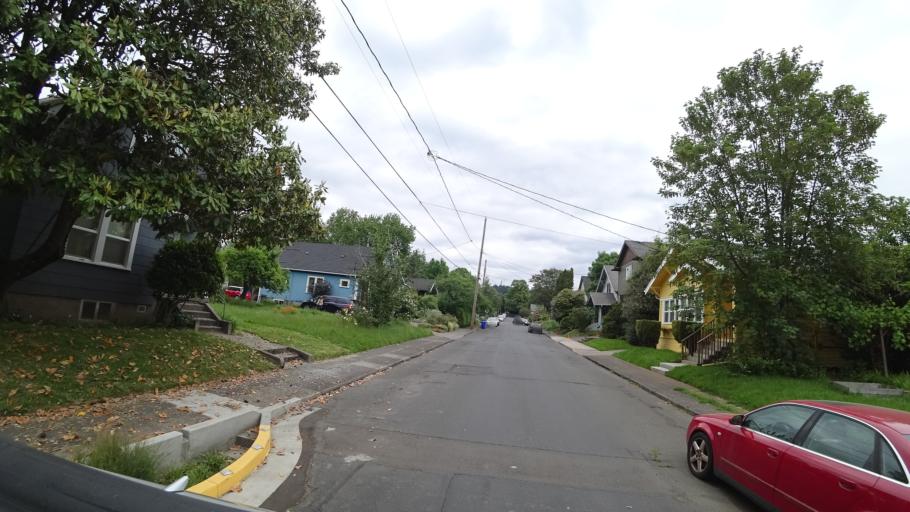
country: US
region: Oregon
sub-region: Multnomah County
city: Lents
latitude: 45.5153
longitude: -122.6151
